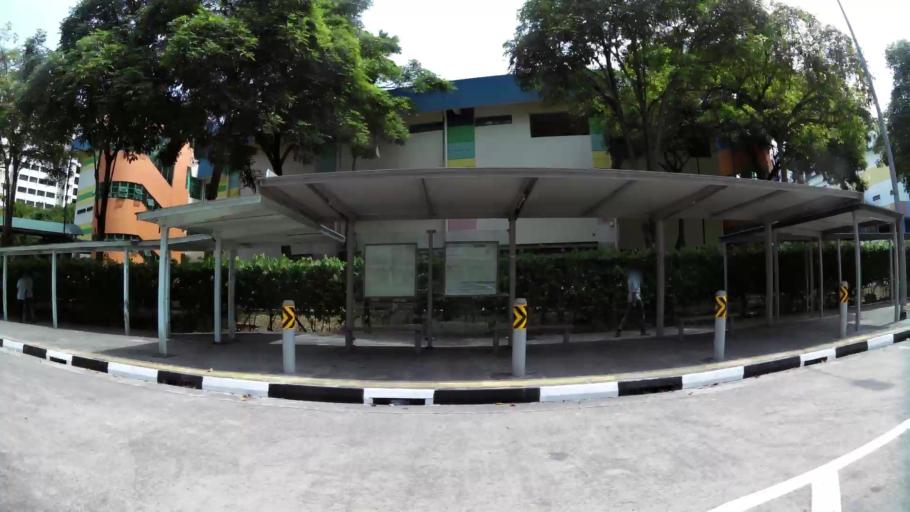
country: MY
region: Johor
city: Johor Bahru
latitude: 1.3393
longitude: 103.6983
